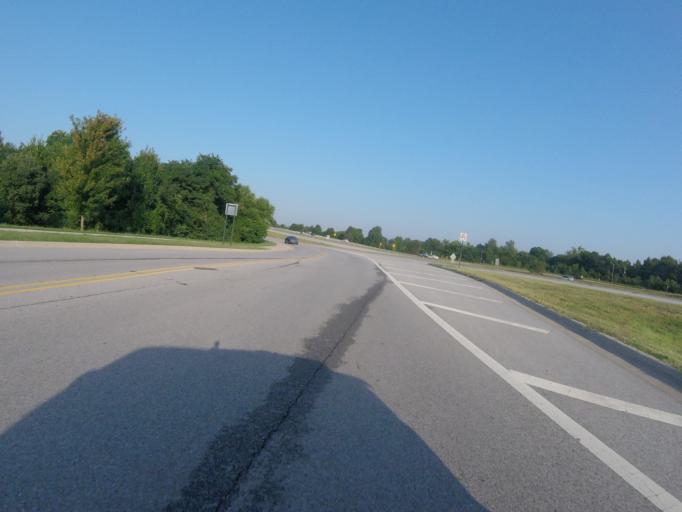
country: US
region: Arkansas
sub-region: Washington County
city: Johnson
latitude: 36.1120
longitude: -94.1590
